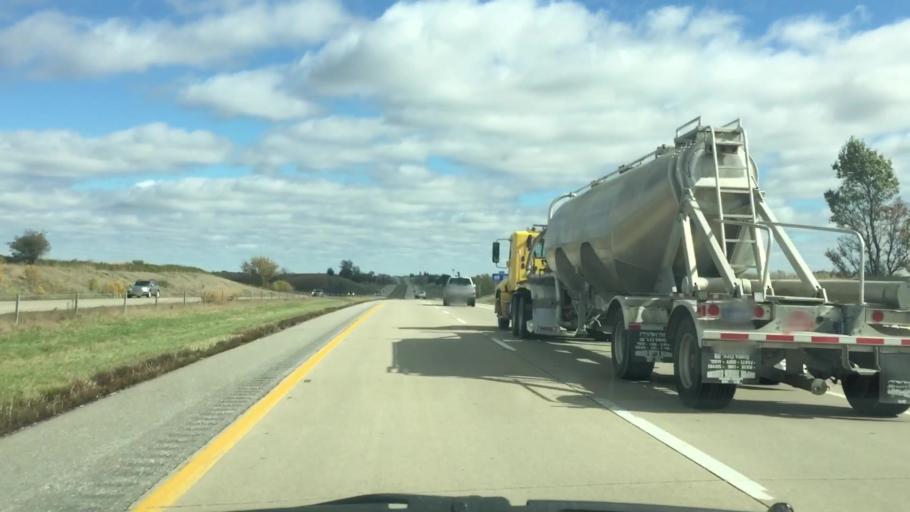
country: US
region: Iowa
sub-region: Poweshiek County
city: Brooklyn
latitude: 41.6960
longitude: -92.3936
